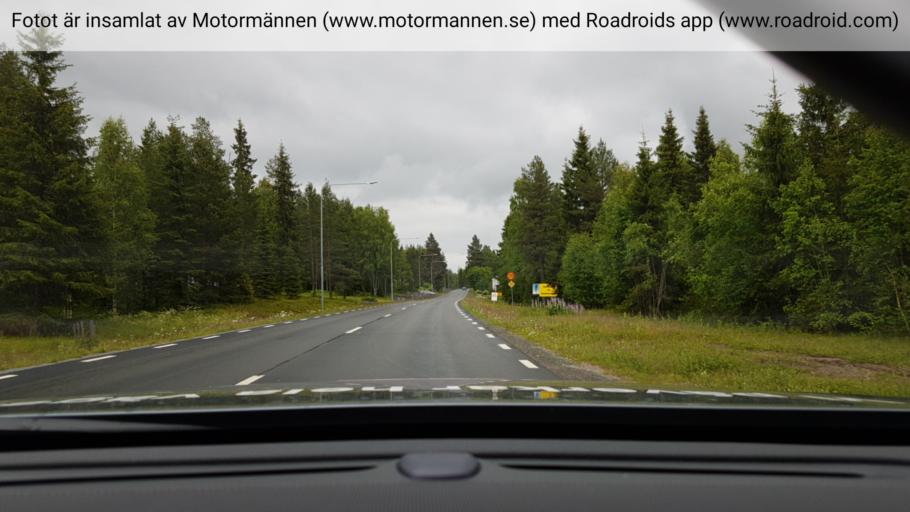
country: SE
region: Vaesterbotten
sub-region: Norsjo Kommun
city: Norsjoe
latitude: 65.2705
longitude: 19.6095
